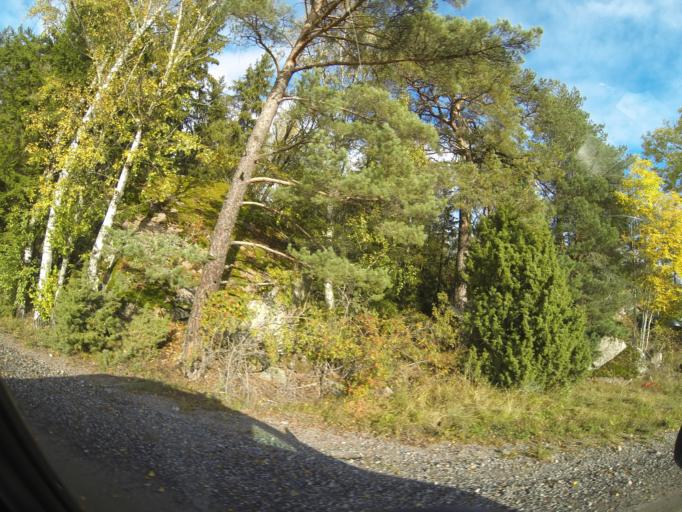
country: SE
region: Soedermanland
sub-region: Eskilstuna Kommun
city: Kvicksund
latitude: 59.3750
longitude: 16.2644
